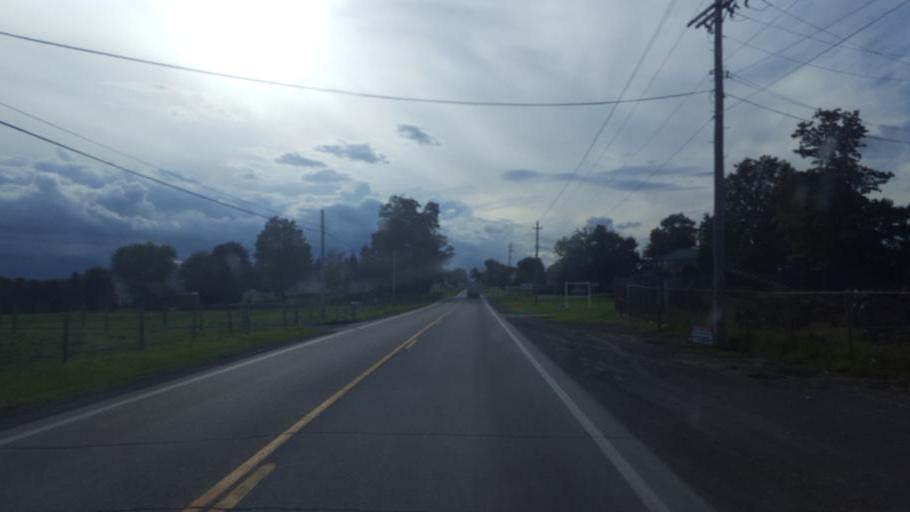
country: US
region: Ohio
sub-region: Geauga County
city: Middlefield
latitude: 41.4594
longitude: -81.0344
